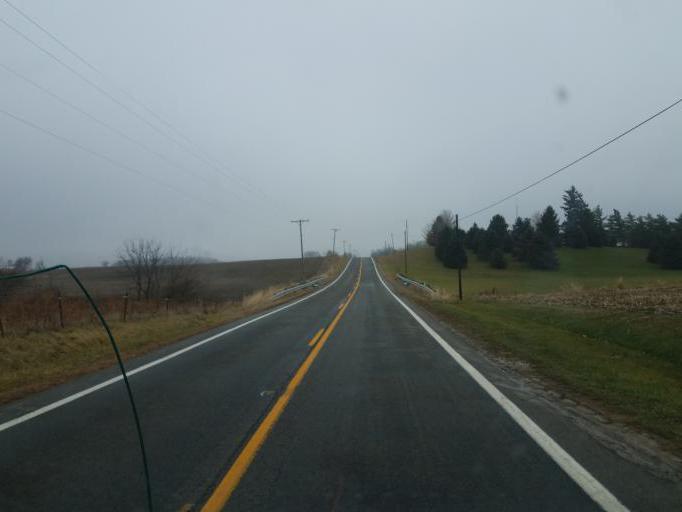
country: US
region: Ohio
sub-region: Champaign County
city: North Lewisburg
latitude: 40.2507
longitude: -83.5775
